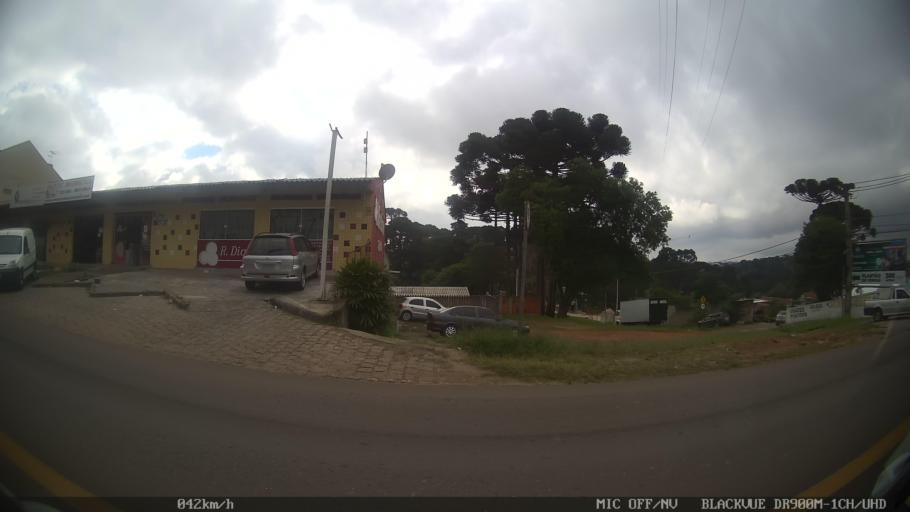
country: BR
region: Parana
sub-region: Curitiba
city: Curitiba
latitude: -25.3690
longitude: -49.2365
